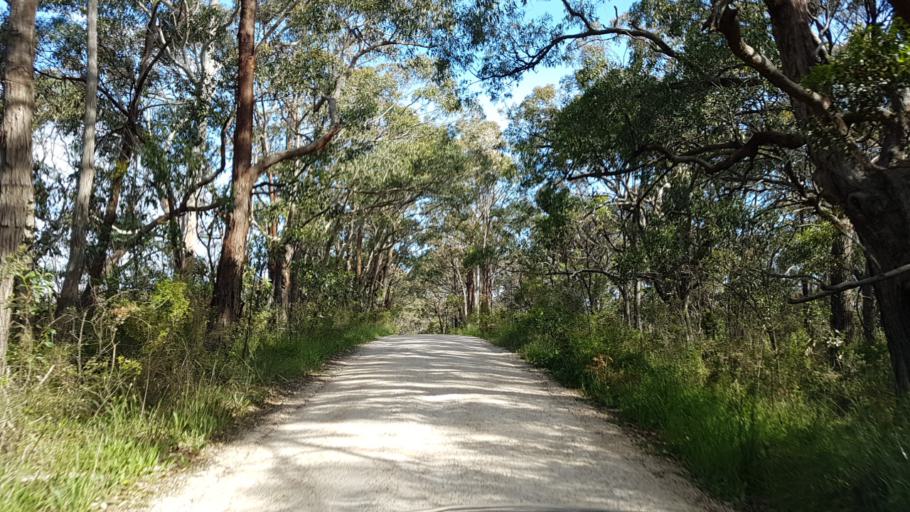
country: AU
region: South Australia
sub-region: Adelaide Hills
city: Adelaide Hills
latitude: -34.9073
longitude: 138.7481
